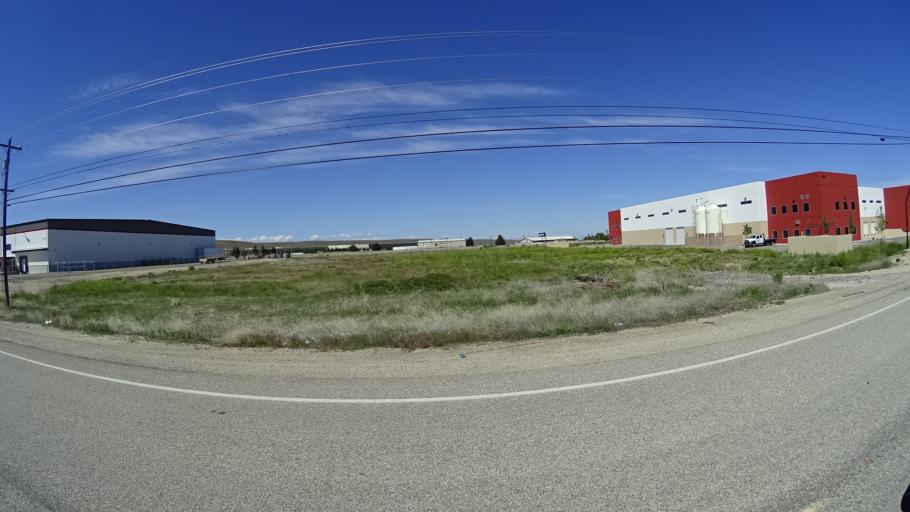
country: US
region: Idaho
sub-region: Ada County
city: Boise
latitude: 43.5240
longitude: -116.1480
